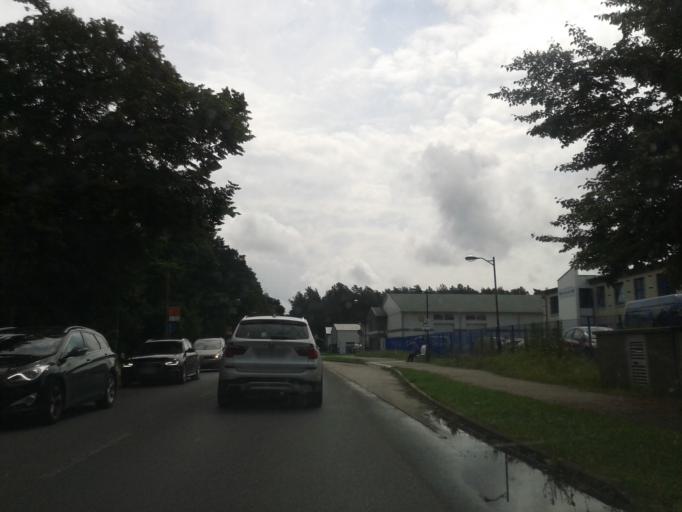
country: DE
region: Mecklenburg-Vorpommern
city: Seebad Heringsdorf
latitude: 53.9330
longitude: 14.1947
